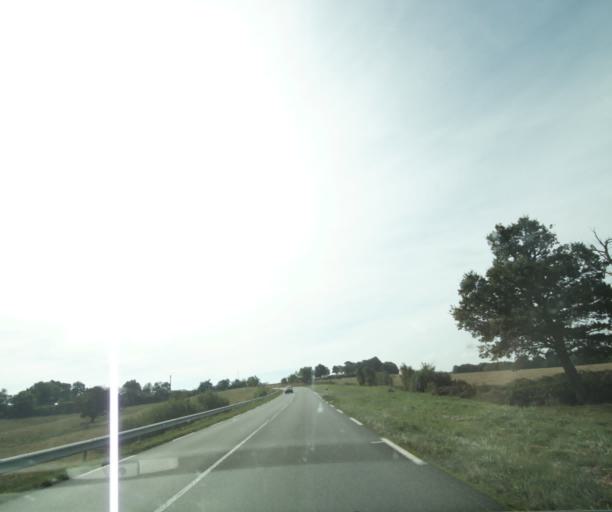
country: FR
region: Auvergne
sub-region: Departement de l'Allier
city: Le Donjon
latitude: 46.3105
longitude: 3.7698
